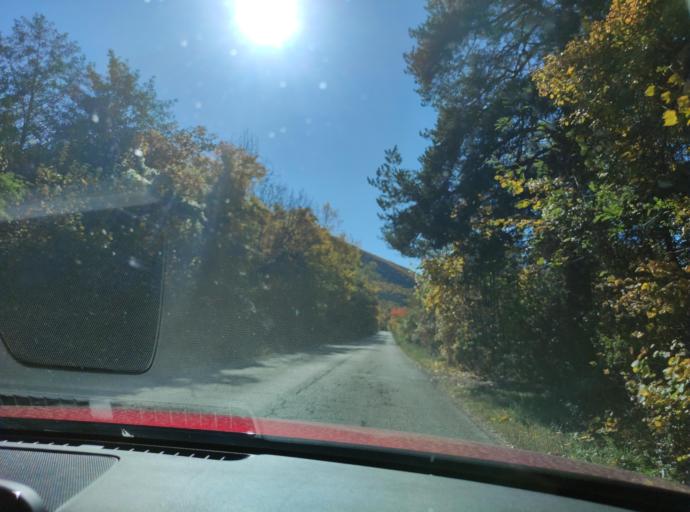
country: BG
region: Montana
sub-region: Obshtina Chiprovtsi
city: Chiprovtsi
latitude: 43.4208
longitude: 22.9542
